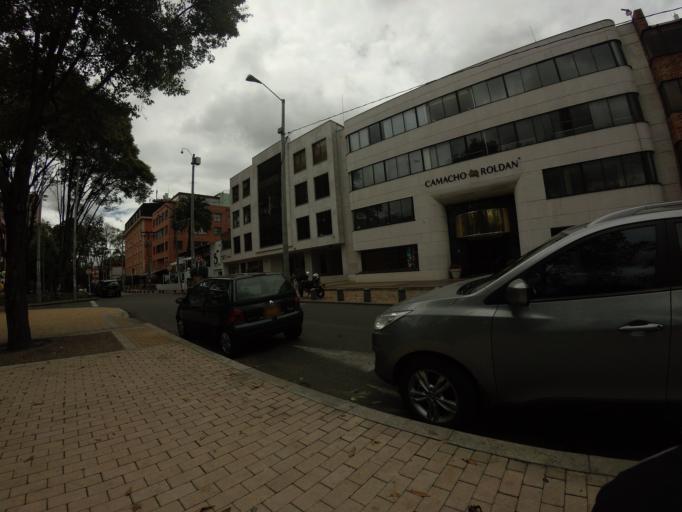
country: CO
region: Bogota D.C.
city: Barrio San Luis
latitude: 4.6766
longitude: -74.0475
